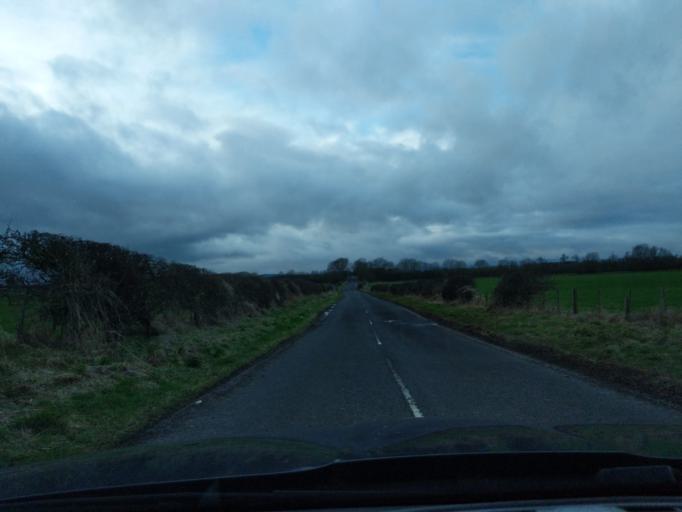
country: GB
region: England
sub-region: Northumberland
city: Ford
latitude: 55.7149
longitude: -2.1304
